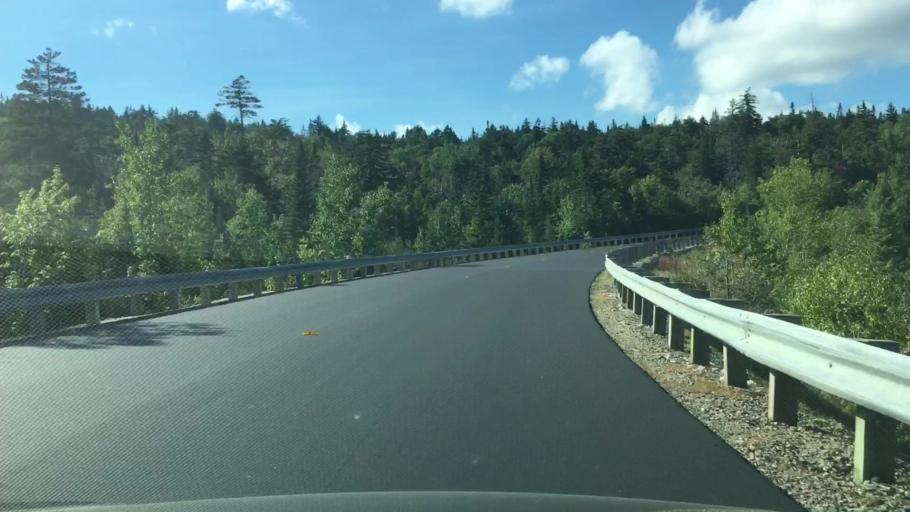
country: US
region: New Hampshire
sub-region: Grafton County
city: Woodstock
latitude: 44.0212
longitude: -71.4914
